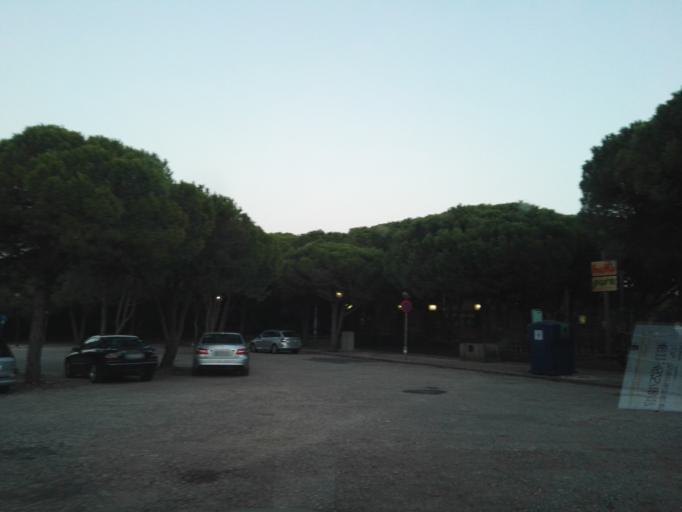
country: PT
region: Lisbon
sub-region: Odivelas
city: Pontinha
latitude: 38.7346
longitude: -9.1796
